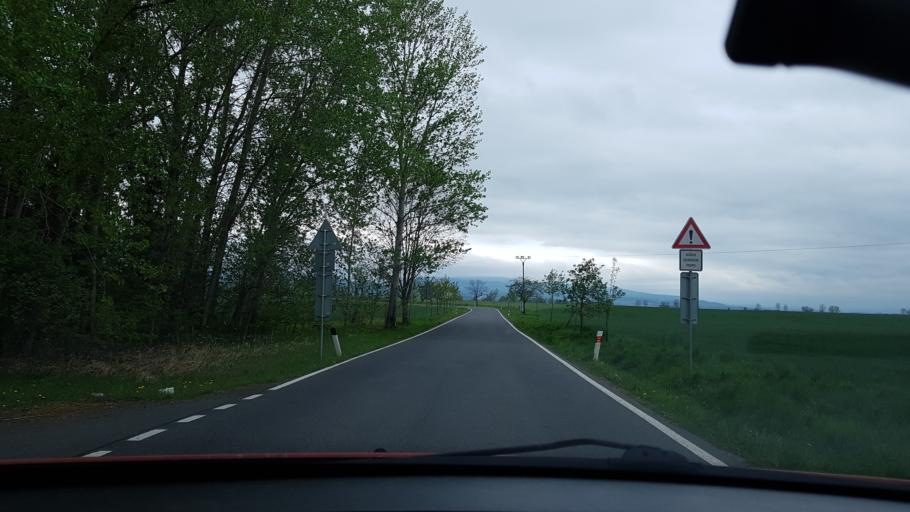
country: CZ
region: Olomoucky
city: Zulova
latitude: 50.3872
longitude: 17.1076
